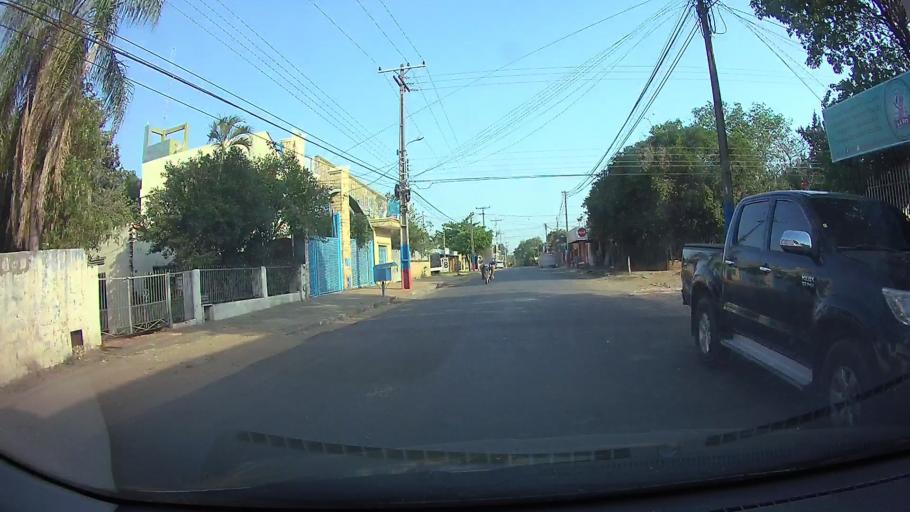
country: PY
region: Central
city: Limpio
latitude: -25.1983
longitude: -57.5073
